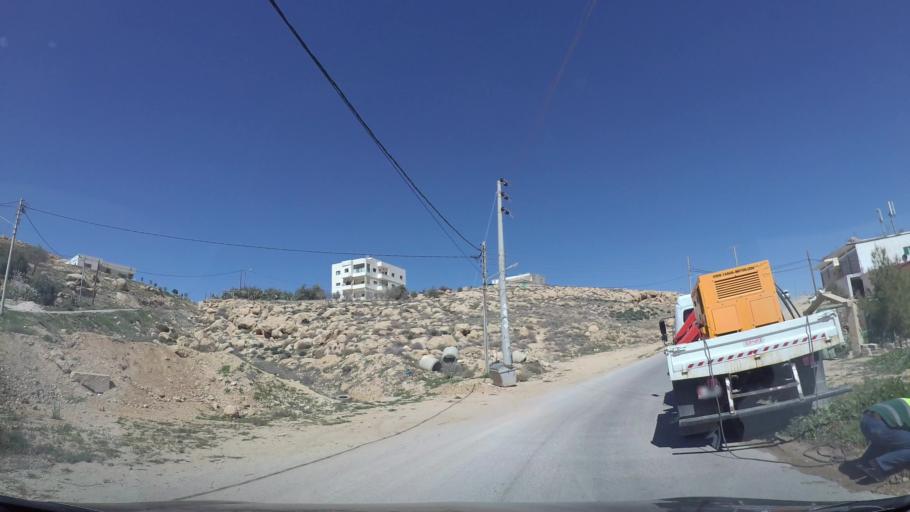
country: JO
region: Tafielah
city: At Tafilah
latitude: 30.8249
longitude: 35.5802
